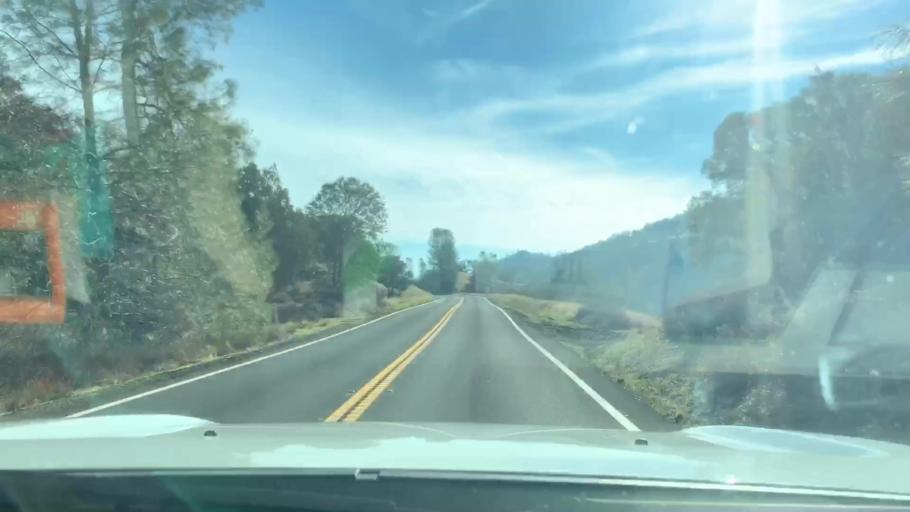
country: US
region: California
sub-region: Fresno County
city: Coalinga
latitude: 36.1130
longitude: -120.5687
